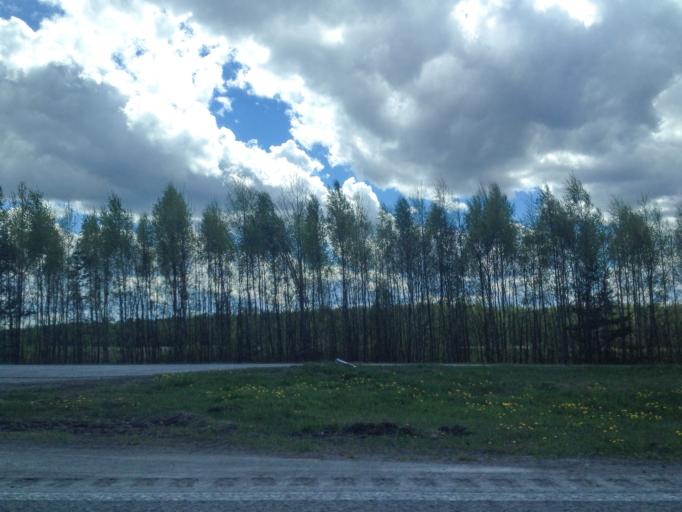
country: FI
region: Haeme
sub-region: Haemeenlinna
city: Parola
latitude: 61.0800
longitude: 24.2650
